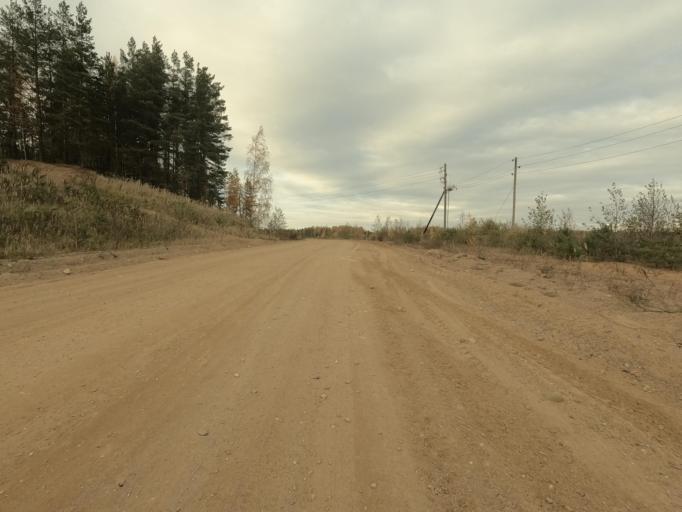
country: RU
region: Leningrad
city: Priladozhskiy
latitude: 59.7086
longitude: 31.3635
